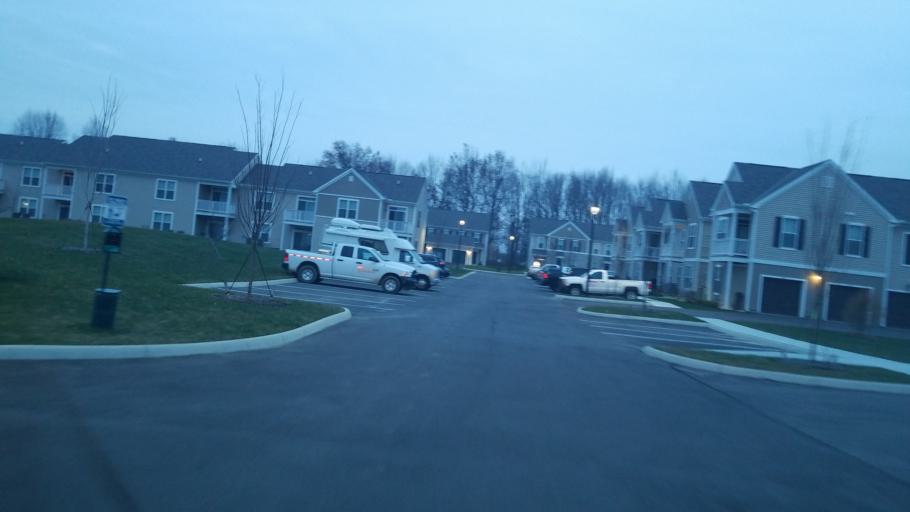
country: US
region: Ohio
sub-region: Delaware County
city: Sunbury
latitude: 40.2698
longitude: -82.9318
